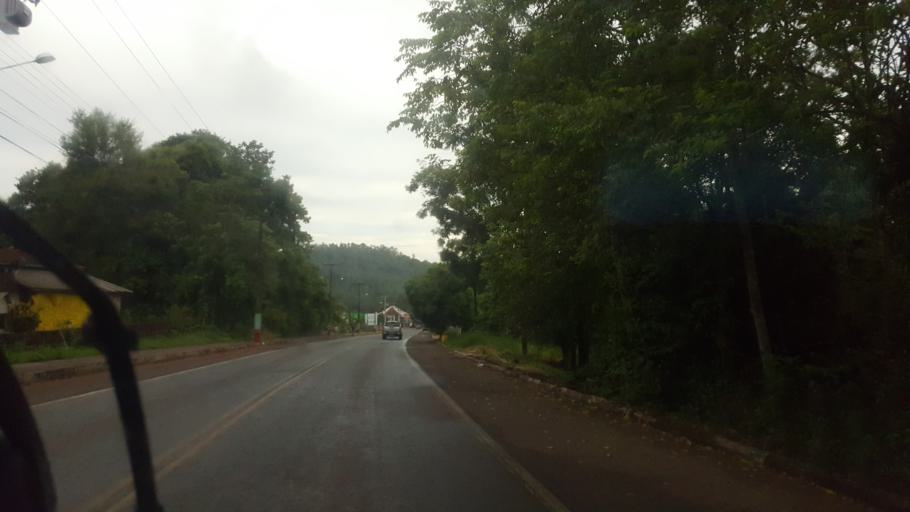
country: BR
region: Rio Grande do Sul
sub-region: Frederico Westphalen
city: Frederico Westphalen
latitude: -27.0935
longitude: -53.3856
